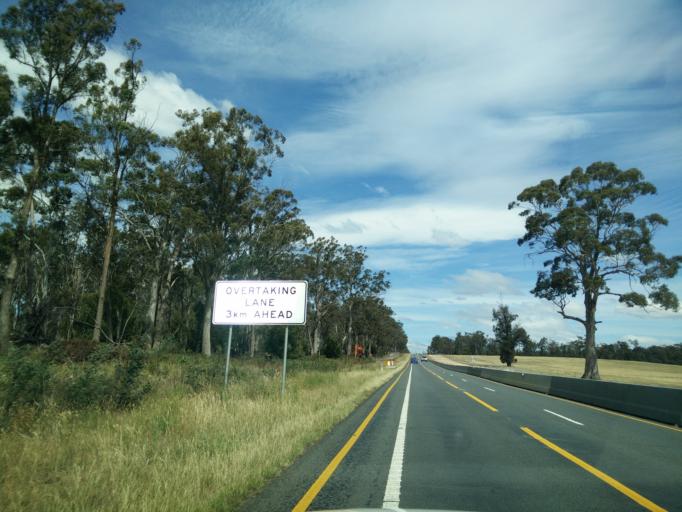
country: AU
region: Tasmania
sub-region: Northern Midlands
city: Evandale
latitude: -41.7462
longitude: 147.3375
